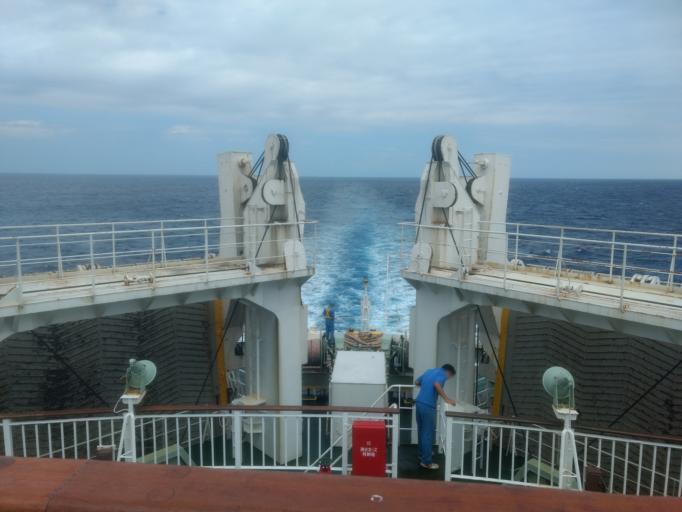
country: JP
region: Kagoshima
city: Nishinoomote
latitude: 30.5096
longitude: 130.6109
